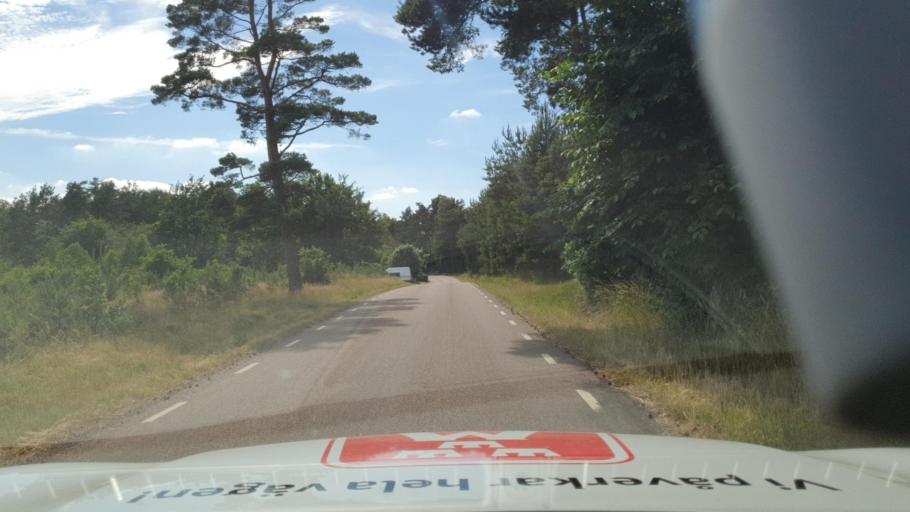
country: SE
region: Skane
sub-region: Sjobo Kommun
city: Blentarp
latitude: 55.6074
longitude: 13.6165
